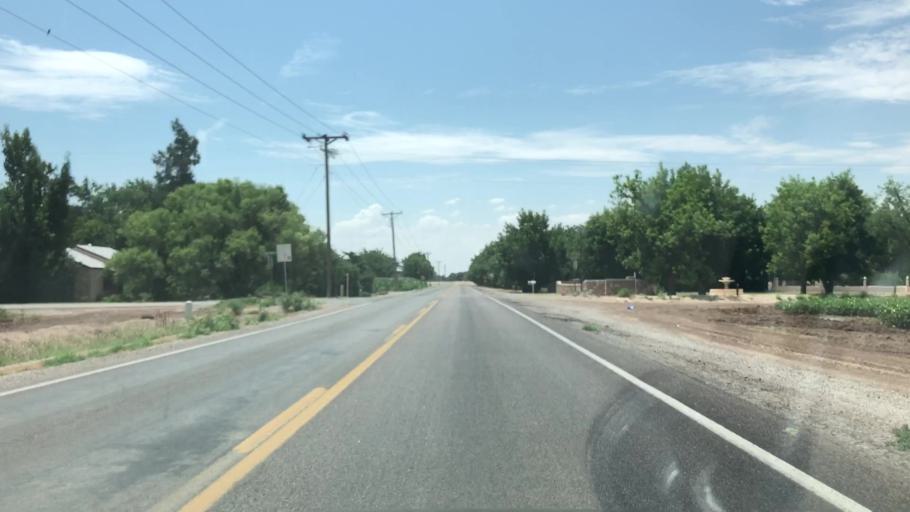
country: US
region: New Mexico
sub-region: Dona Ana County
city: Vado
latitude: 32.0976
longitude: -106.6836
